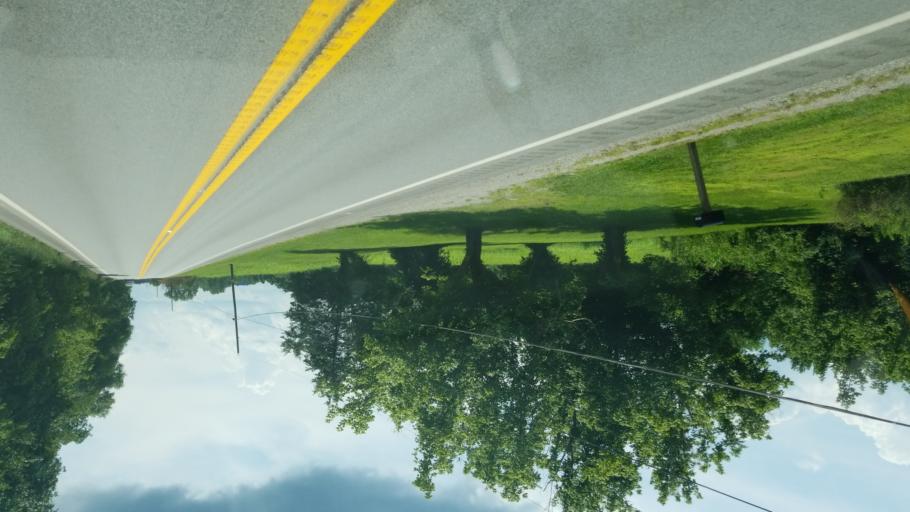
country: US
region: West Virginia
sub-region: Putnam County
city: Buffalo
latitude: 38.6154
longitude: -81.9917
